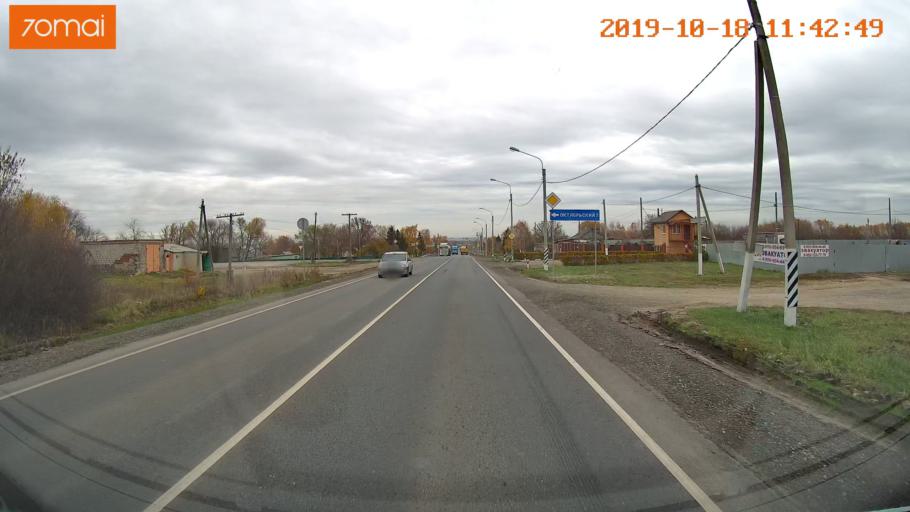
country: RU
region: Rjazan
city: Oktyabr'skiy
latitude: 54.1920
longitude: 38.9349
